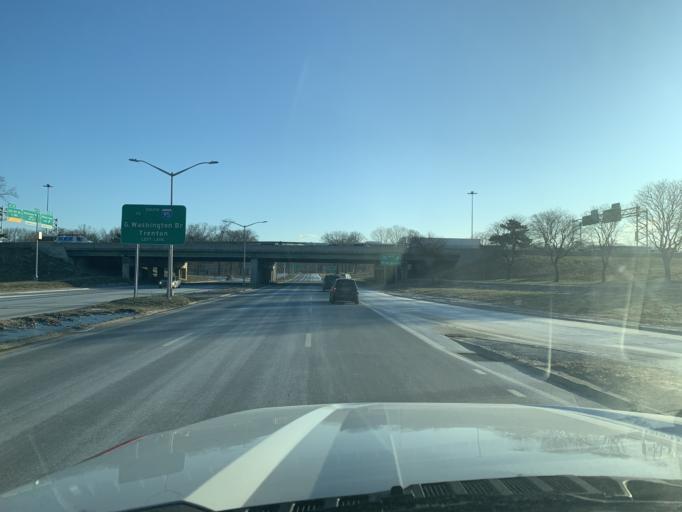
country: US
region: New York
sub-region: Bronx
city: Eastchester
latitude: 40.8564
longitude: -73.8277
